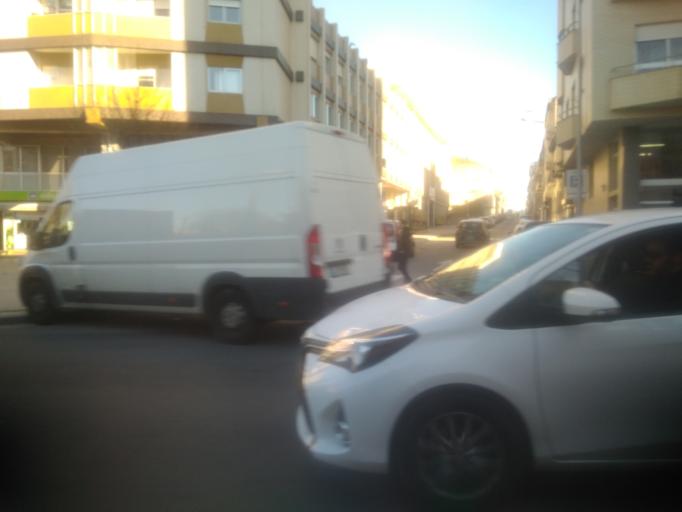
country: PT
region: Porto
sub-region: Vila Nova de Gaia
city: Vila Nova de Gaia
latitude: 41.1356
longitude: -8.6079
